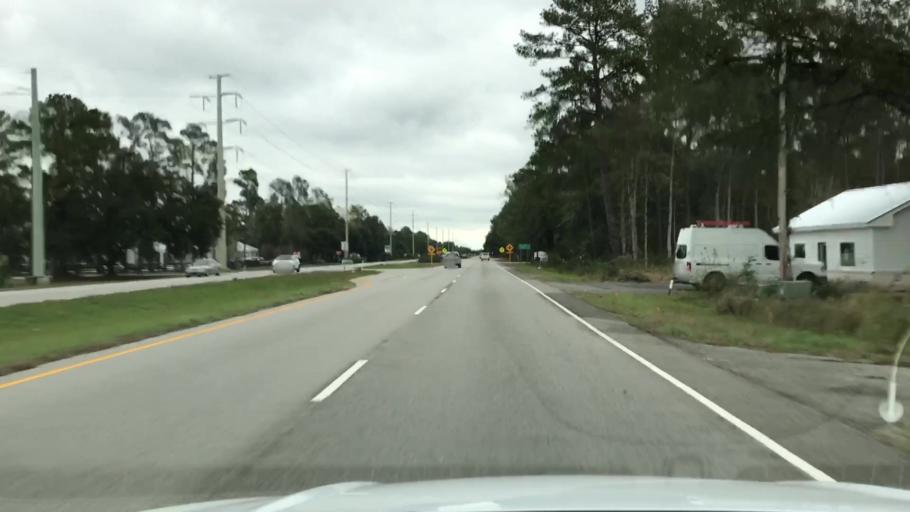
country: US
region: South Carolina
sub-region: Georgetown County
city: Georgetown
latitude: 33.4198
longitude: -79.1770
